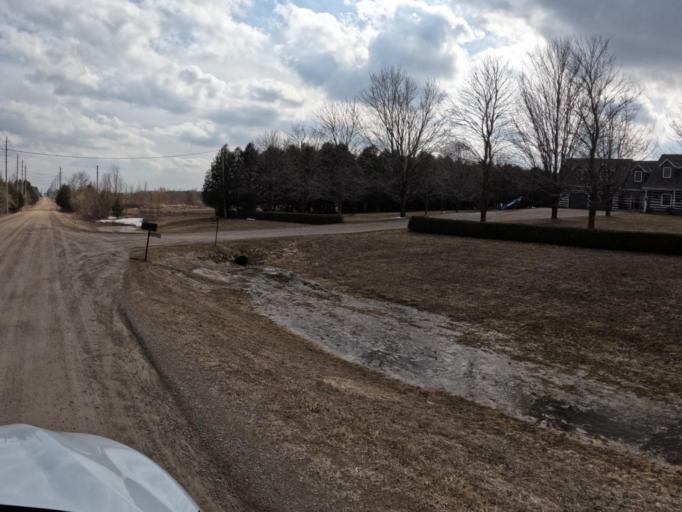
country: CA
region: Ontario
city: Shelburne
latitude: 43.9735
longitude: -80.3020
